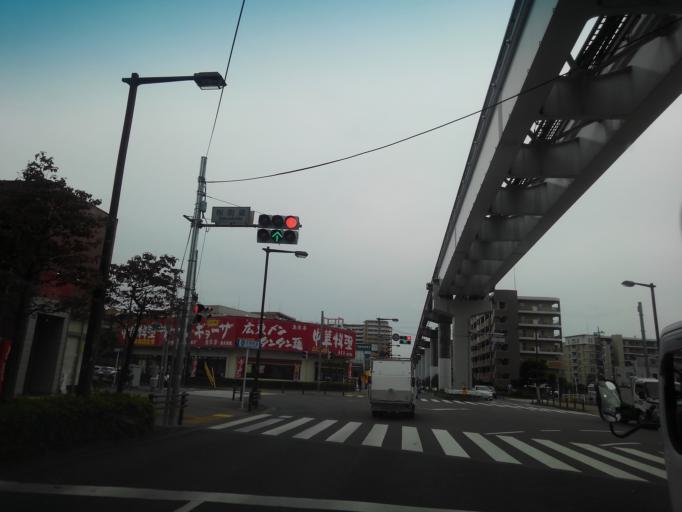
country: JP
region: Tokyo
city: Higashimurayama-shi
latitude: 35.7390
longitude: 139.4167
